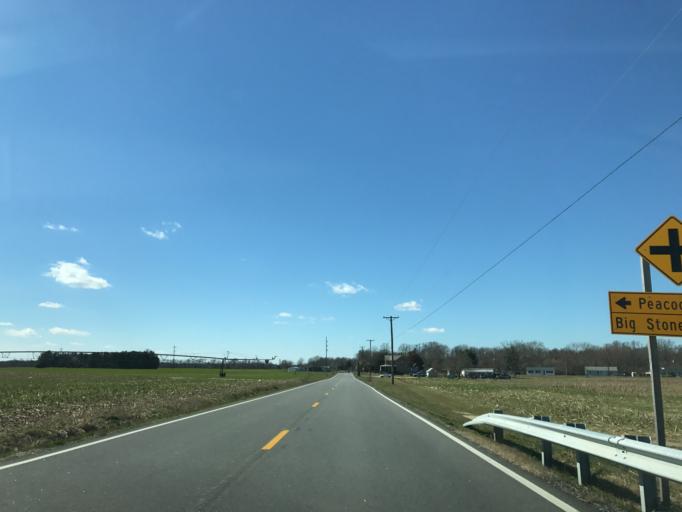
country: US
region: Delaware
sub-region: Kent County
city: Clayton
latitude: 39.2547
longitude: -75.8085
